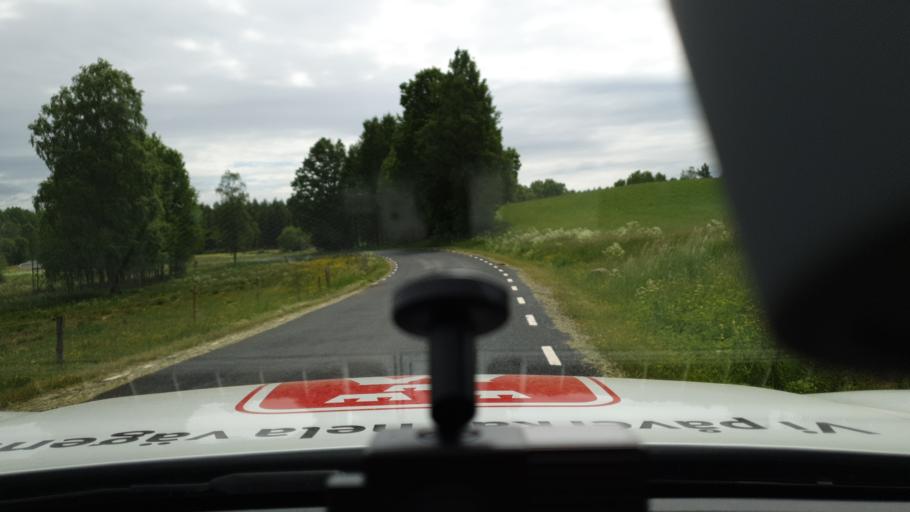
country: SE
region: Joenkoeping
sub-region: Mullsjo Kommun
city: Mullsjoe
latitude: 57.9918
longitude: 13.7411
